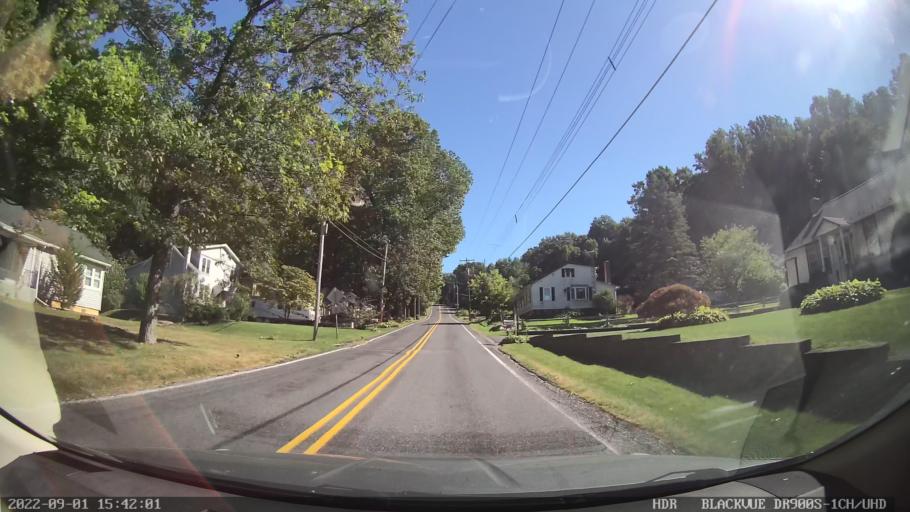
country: US
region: Pennsylvania
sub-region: Berks County
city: Topton
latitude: 40.4932
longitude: -75.7007
